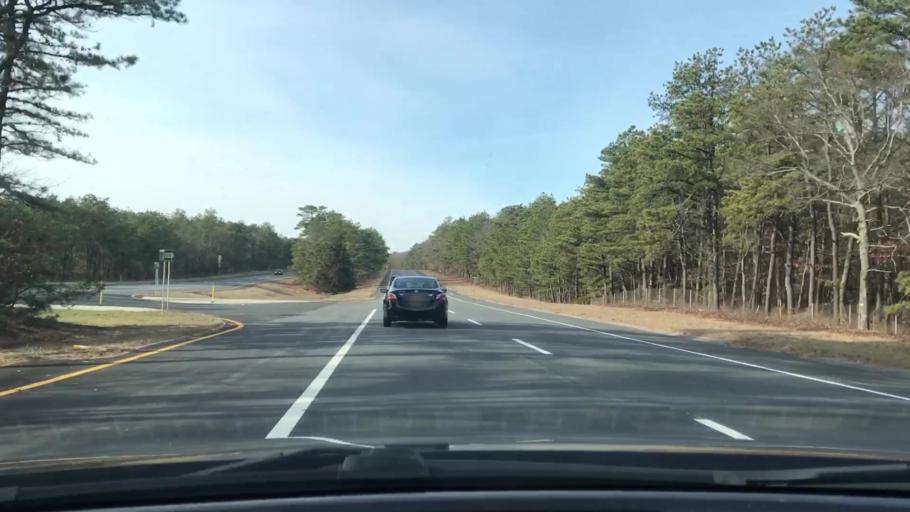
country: US
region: New York
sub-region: Suffolk County
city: Calverton
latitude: 40.9068
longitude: -72.7083
